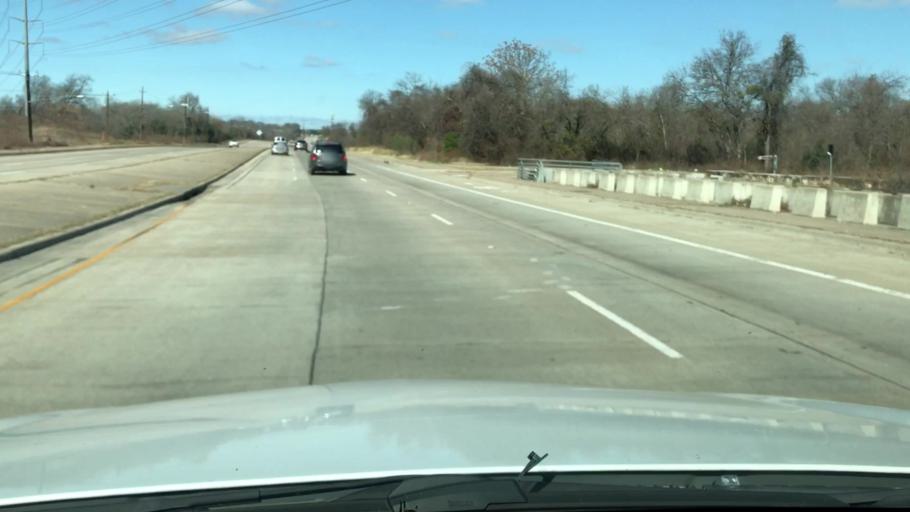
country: US
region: Texas
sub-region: Travis County
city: Onion Creek
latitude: 30.1715
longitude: -97.7396
